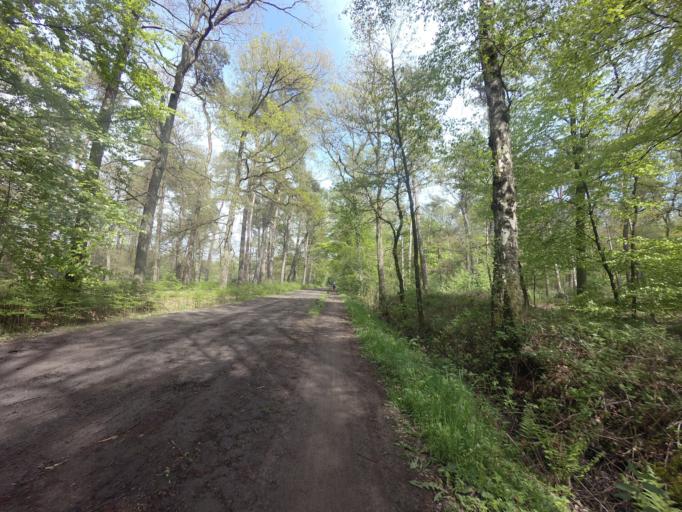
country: NL
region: Overijssel
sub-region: Gemeente Haaksbergen
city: Haaksbergen
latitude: 52.1319
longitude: 6.7177
